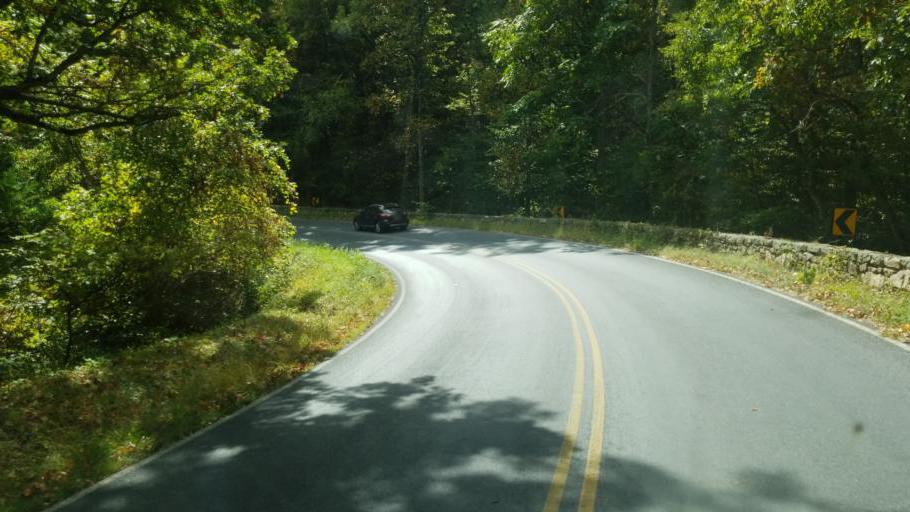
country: US
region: Virginia
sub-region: Warren County
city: Front Royal
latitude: 38.8892
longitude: -78.1968
